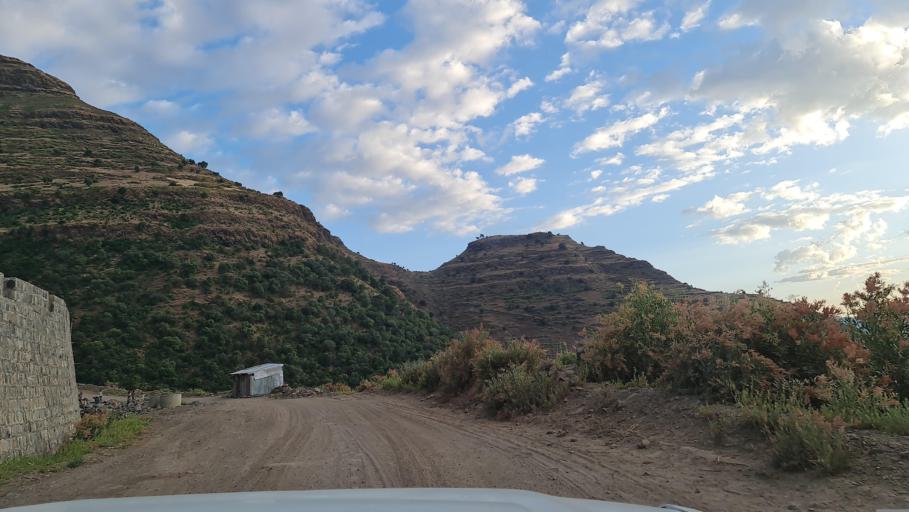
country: ET
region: Amhara
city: Debark'
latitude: 13.0119
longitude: 38.0463
